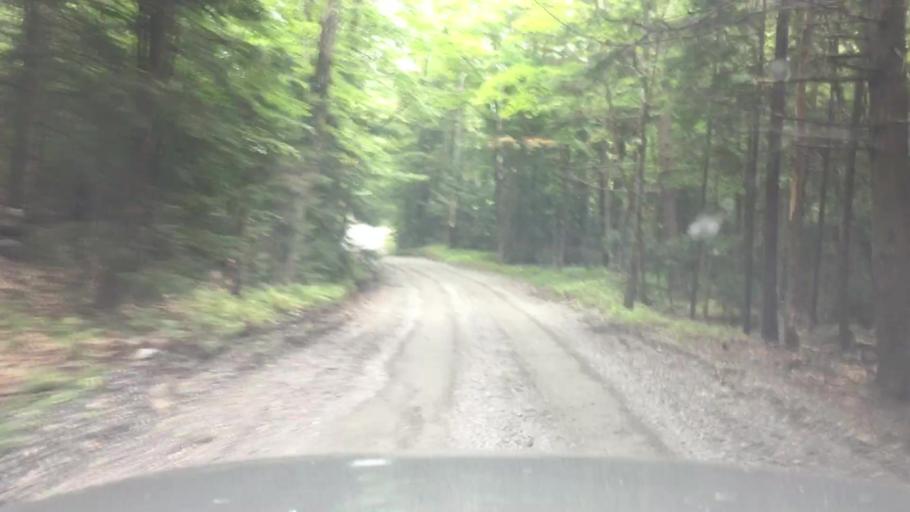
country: US
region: Vermont
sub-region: Windham County
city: Dover
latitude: 42.8331
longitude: -72.7683
